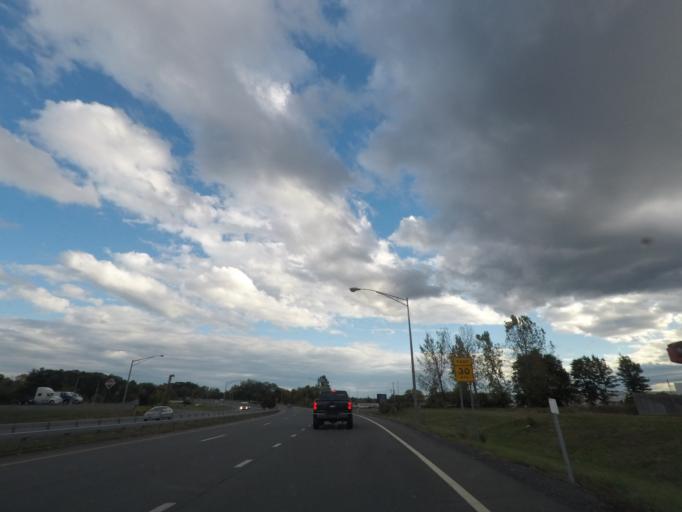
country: US
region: New York
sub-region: Albany County
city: McKownville
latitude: 42.6924
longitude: -73.8497
